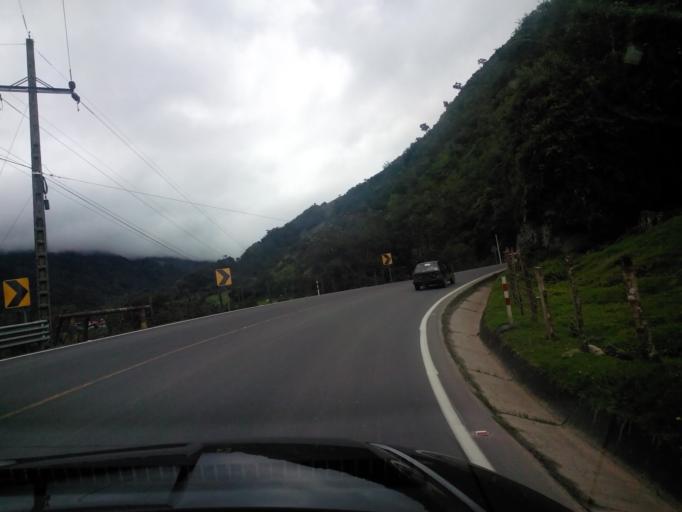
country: EC
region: Pichincha
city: Sangolqui
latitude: -0.3764
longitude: -78.1225
